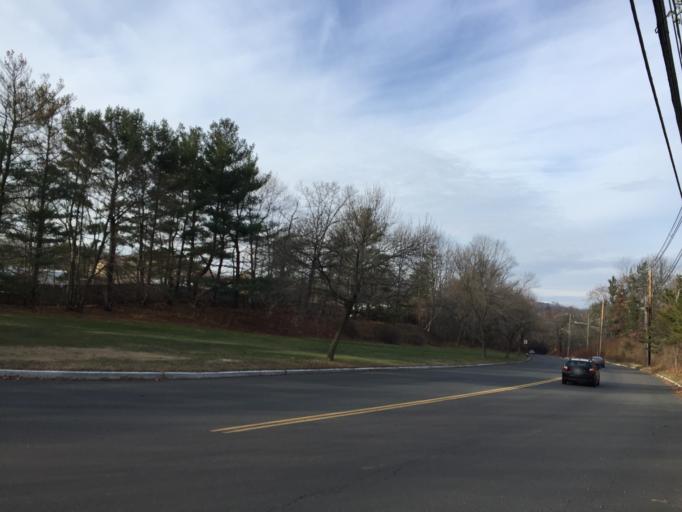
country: US
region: New Jersey
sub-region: Union County
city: Springfield
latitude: 40.7108
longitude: -74.3327
